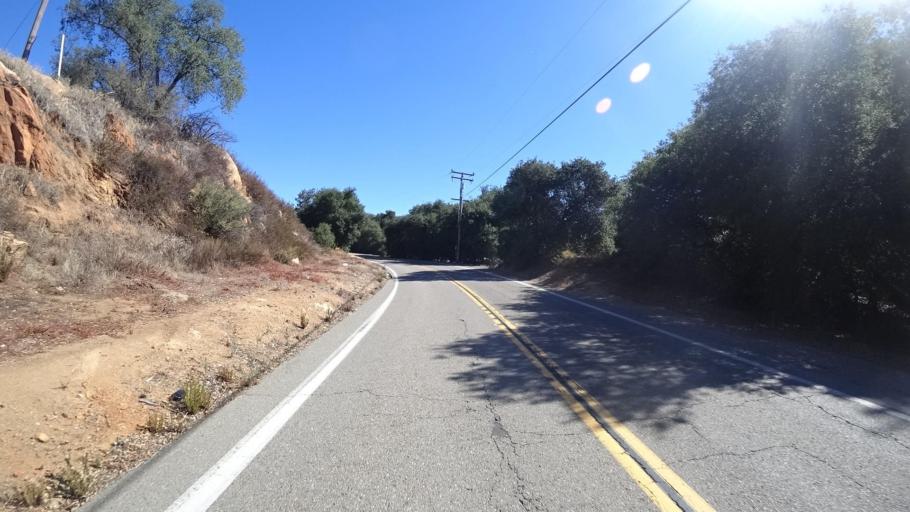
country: US
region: California
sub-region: San Diego County
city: Descanso
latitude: 32.7901
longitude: -116.6612
